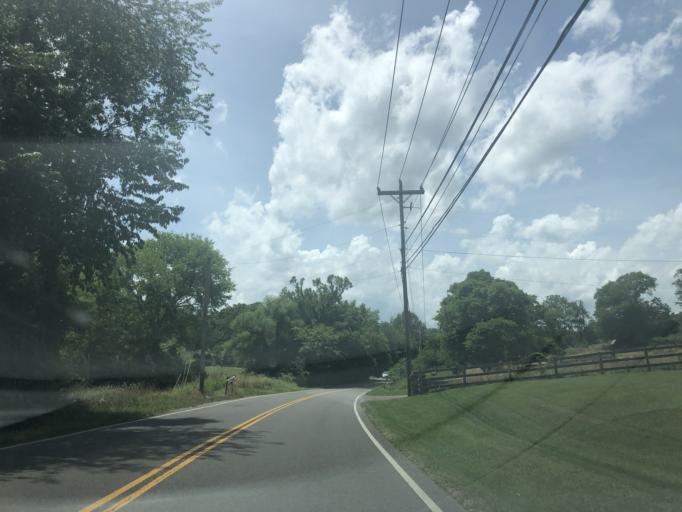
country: US
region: Tennessee
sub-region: Cheatham County
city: Pegram
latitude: 36.0548
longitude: -86.9573
